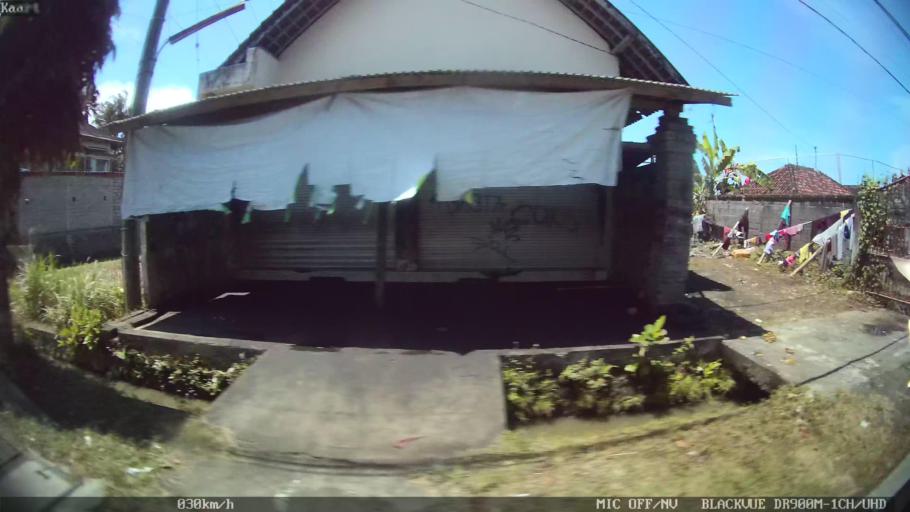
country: ID
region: Bali
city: Banjar Pasekan
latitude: -8.5691
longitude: 115.3216
